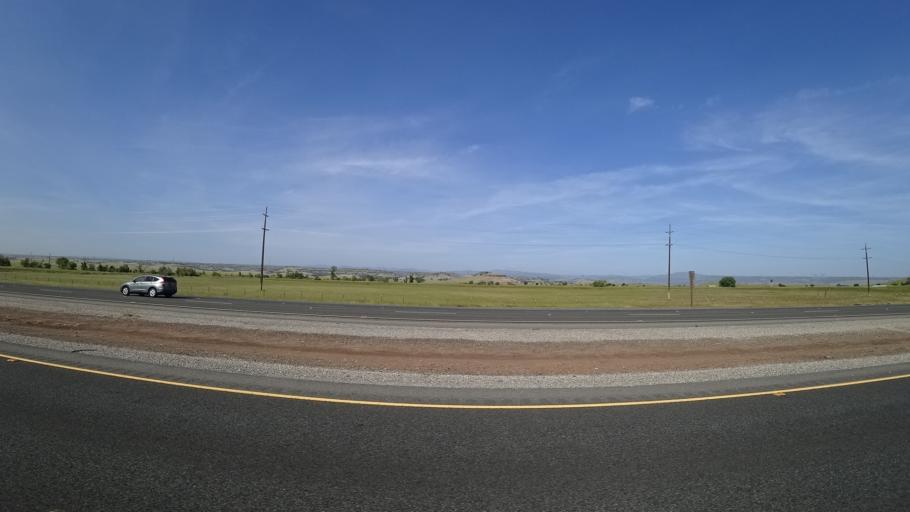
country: US
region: California
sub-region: Butte County
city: Durham
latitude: 39.6300
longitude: -121.7024
